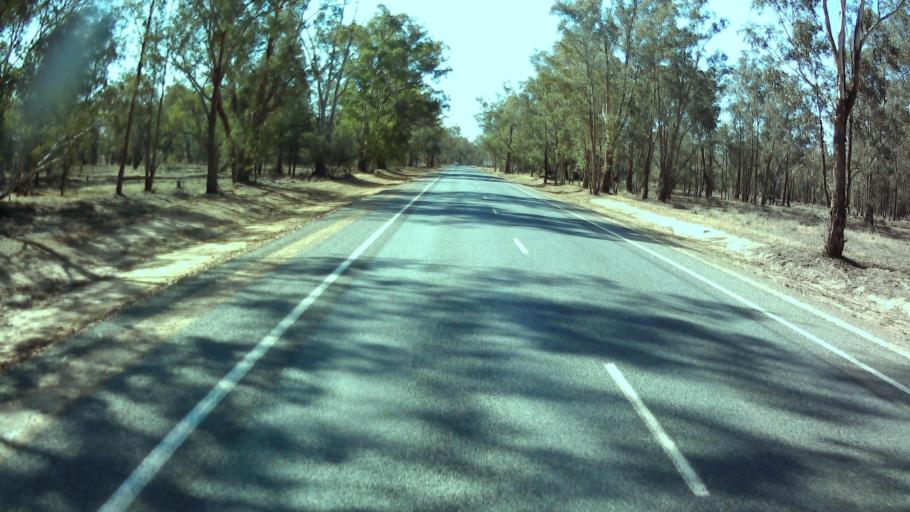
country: AU
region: New South Wales
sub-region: Weddin
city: Grenfell
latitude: -33.7237
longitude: 148.0842
